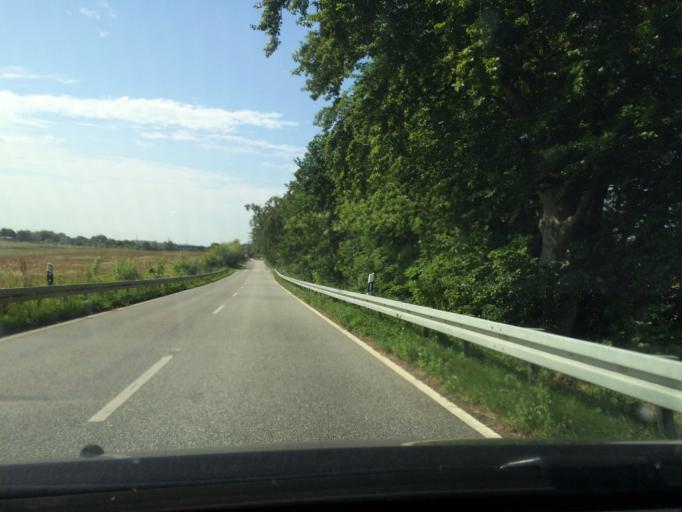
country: DE
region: Mecklenburg-Vorpommern
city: Altefahr
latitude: 54.3291
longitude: 13.1415
